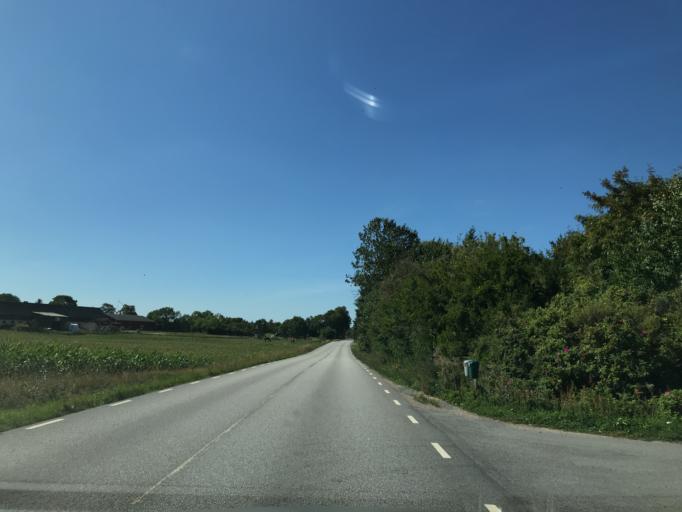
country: SE
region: Skane
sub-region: Tomelilla Kommun
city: Tomelilla
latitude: 55.6550
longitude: 13.9110
